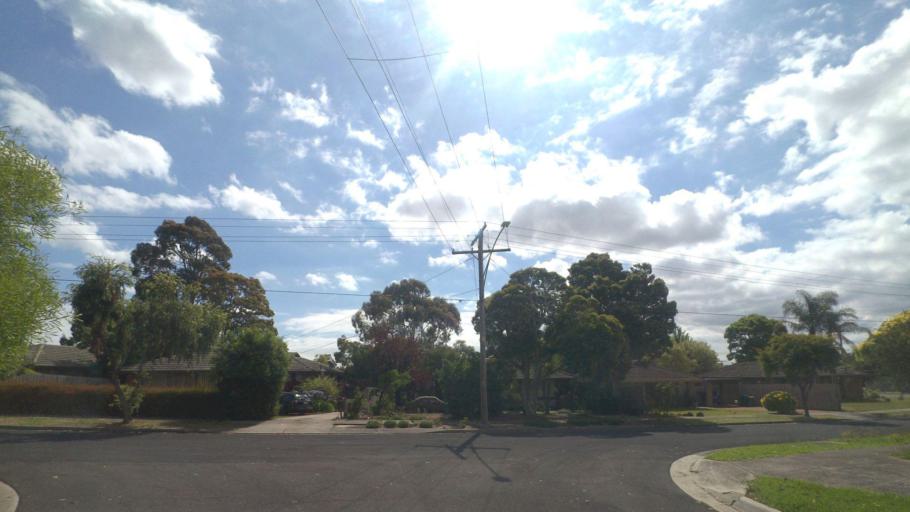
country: AU
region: Victoria
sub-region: Knox
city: Bayswater
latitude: -37.8596
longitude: 145.2568
